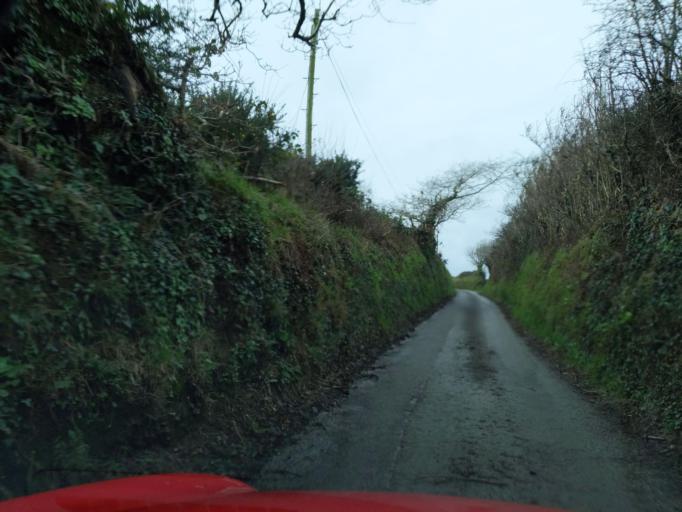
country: GB
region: England
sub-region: Cornwall
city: Duloe
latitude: 50.3490
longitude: -4.5453
